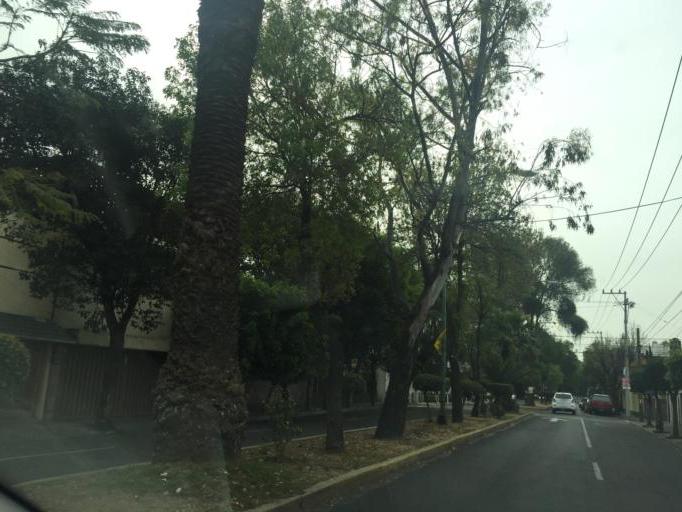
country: MX
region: Mexico
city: Colonia Lindavista
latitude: 19.4930
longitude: -99.1233
